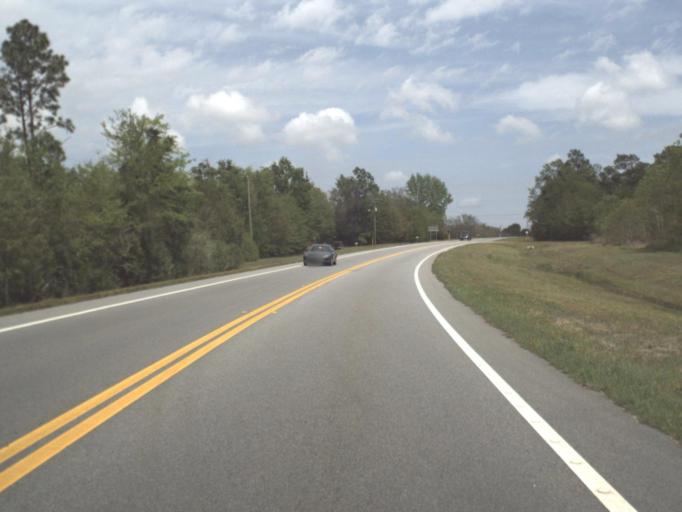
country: US
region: Florida
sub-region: Escambia County
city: Cantonment
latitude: 30.5335
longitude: -87.4232
